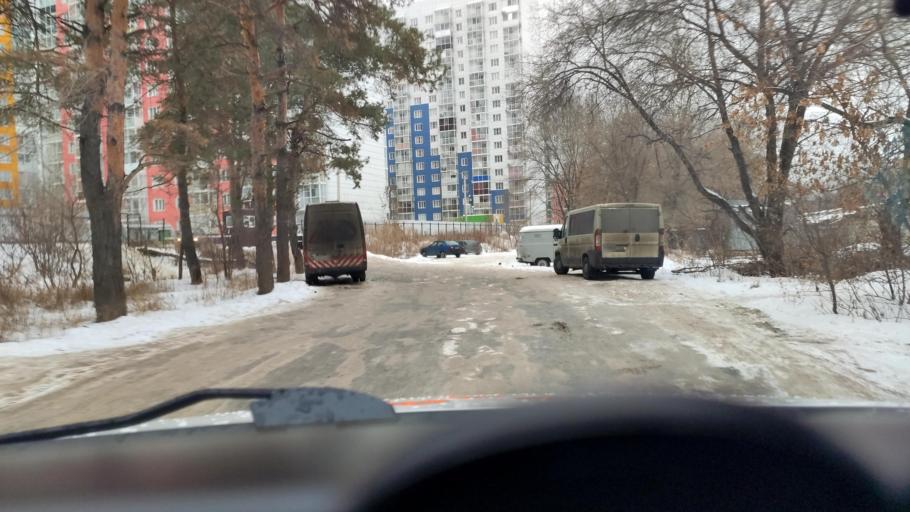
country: RU
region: Voronezj
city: Podgornoye
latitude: 51.6852
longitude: 39.1335
